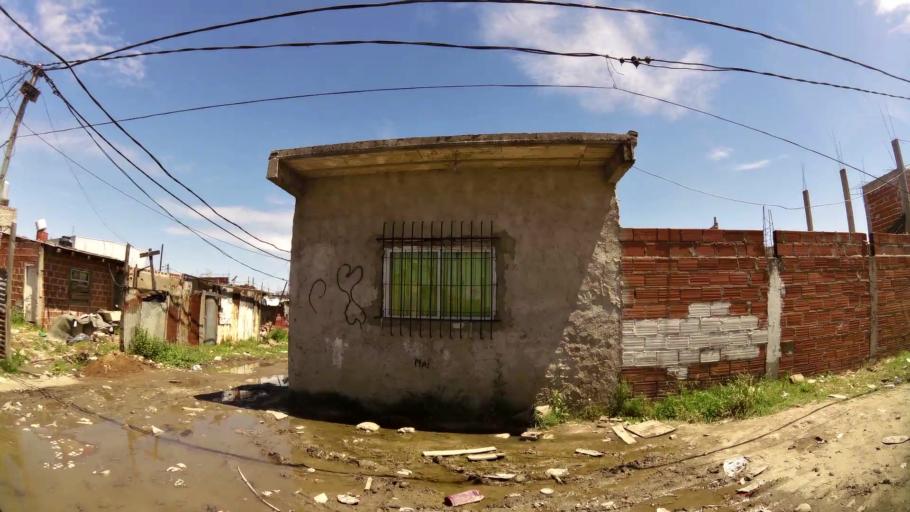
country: AR
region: Buenos Aires
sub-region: Partido de Quilmes
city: Quilmes
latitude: -34.7287
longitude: -58.3161
